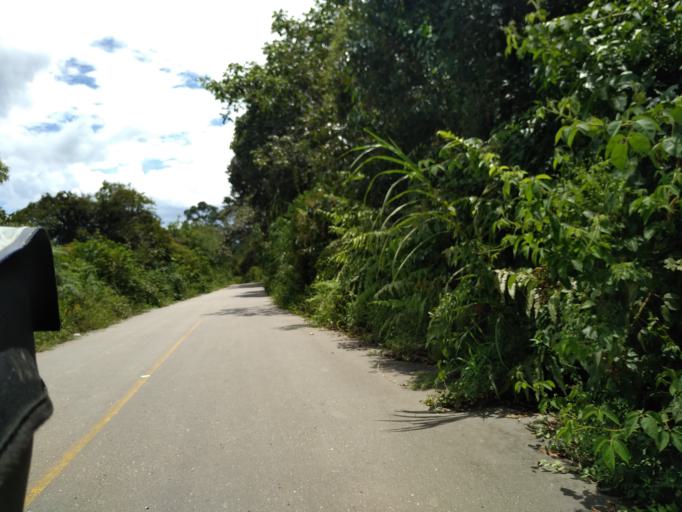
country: CO
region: Santander
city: Oiba
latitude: 6.1909
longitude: -73.1815
